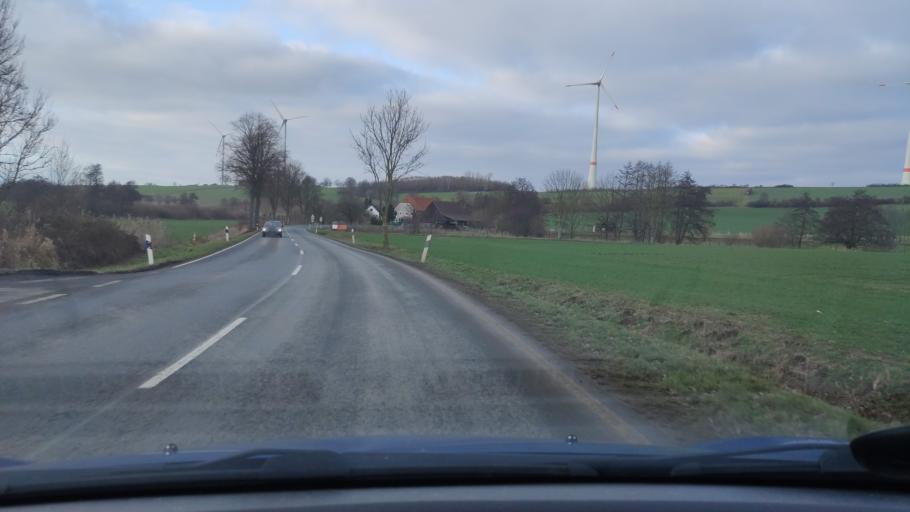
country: DE
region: Lower Saxony
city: Coppenbrugge
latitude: 52.1307
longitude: 9.5416
